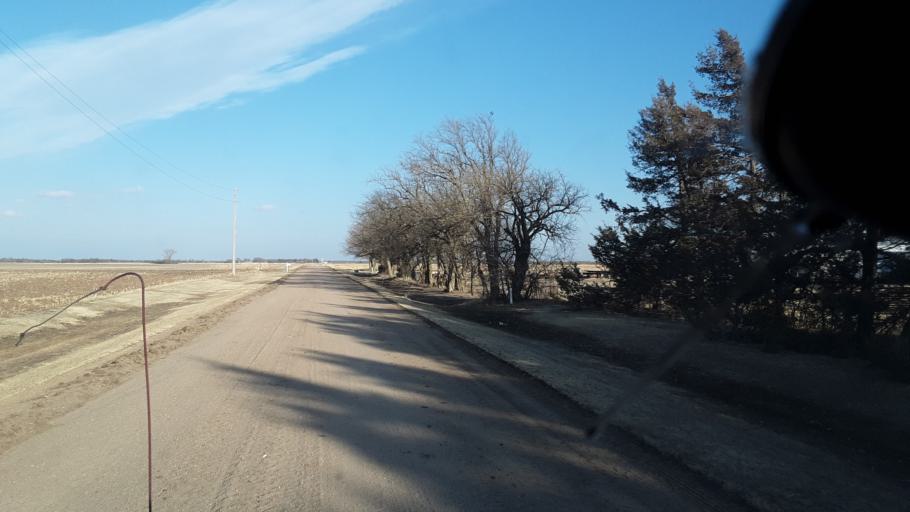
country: US
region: Kansas
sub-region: Reno County
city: South Hutchinson
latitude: 37.9843
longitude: -97.9697
